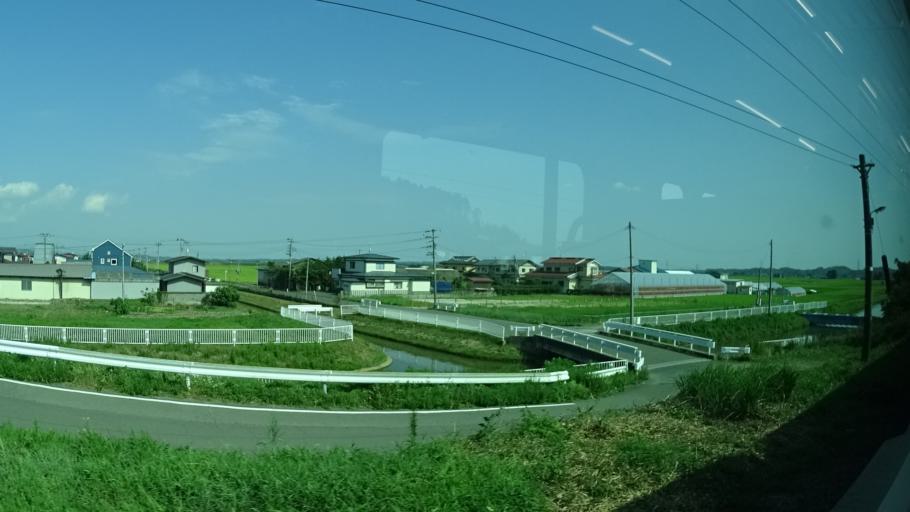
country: JP
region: Miyagi
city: Wakuya
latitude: 38.4728
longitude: 141.0979
